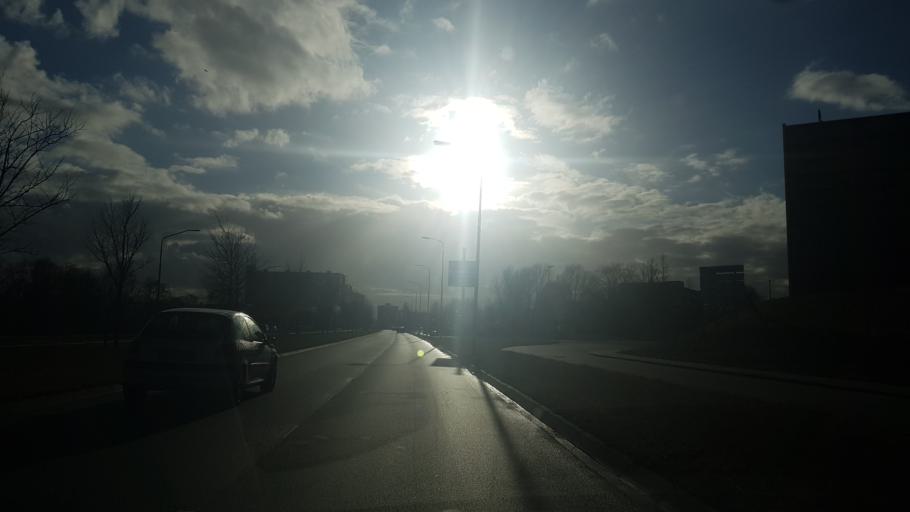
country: NL
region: Friesland
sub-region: Gemeente Leeuwarden
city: Leeuwarden
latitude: 53.2159
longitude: 5.8234
